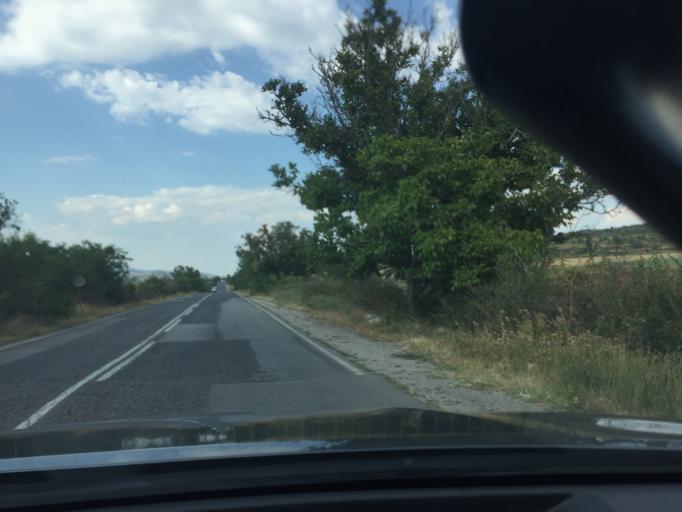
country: BG
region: Kyustendil
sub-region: Obshtina Boboshevo
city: Boboshevo
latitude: 42.1297
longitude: 23.0397
